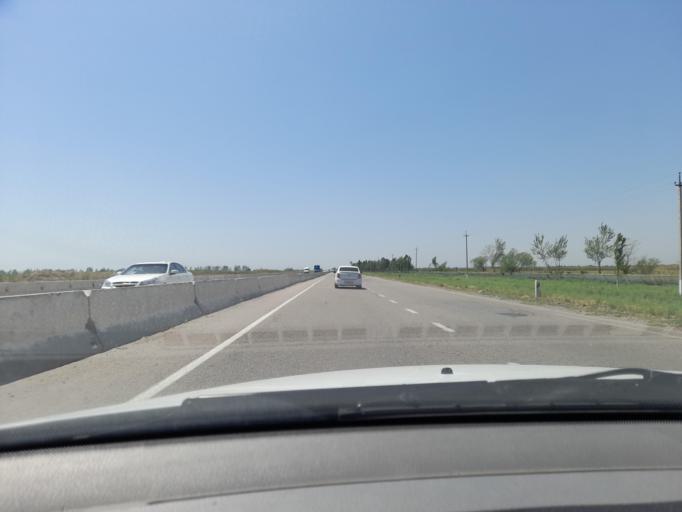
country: UZ
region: Jizzax
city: Dustlik
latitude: 40.4338
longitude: 68.2290
